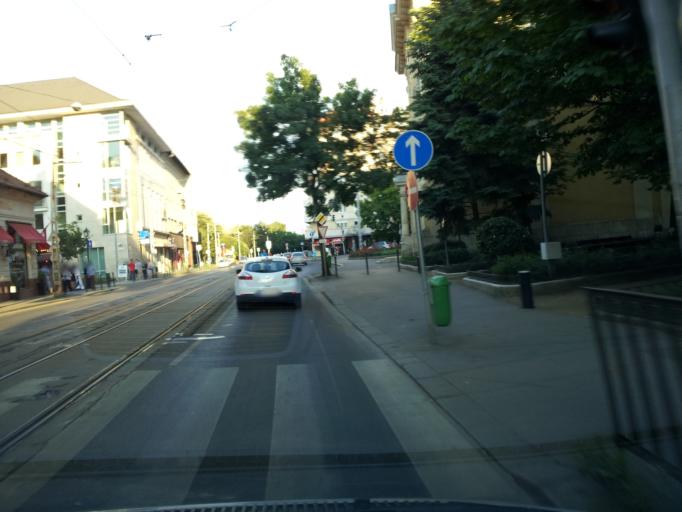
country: HU
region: Budapest
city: Budapest I. keruelet
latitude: 47.4974
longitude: 19.0313
